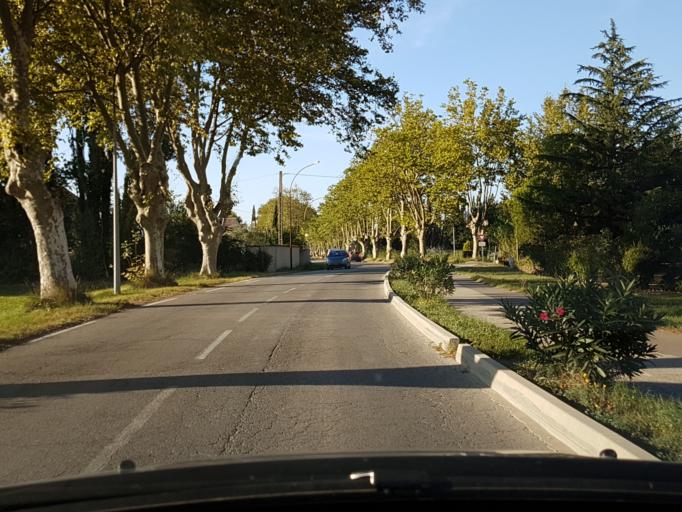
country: FR
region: Provence-Alpes-Cote d'Azur
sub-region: Departement des Bouches-du-Rhone
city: Saint-Andiol
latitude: 43.8256
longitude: 4.9459
